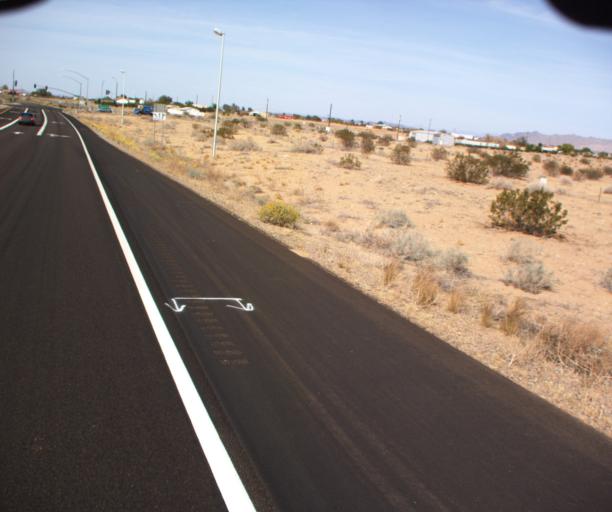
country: US
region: Arizona
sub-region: Yuma County
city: Fortuna Foothills
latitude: 32.6247
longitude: -114.5199
